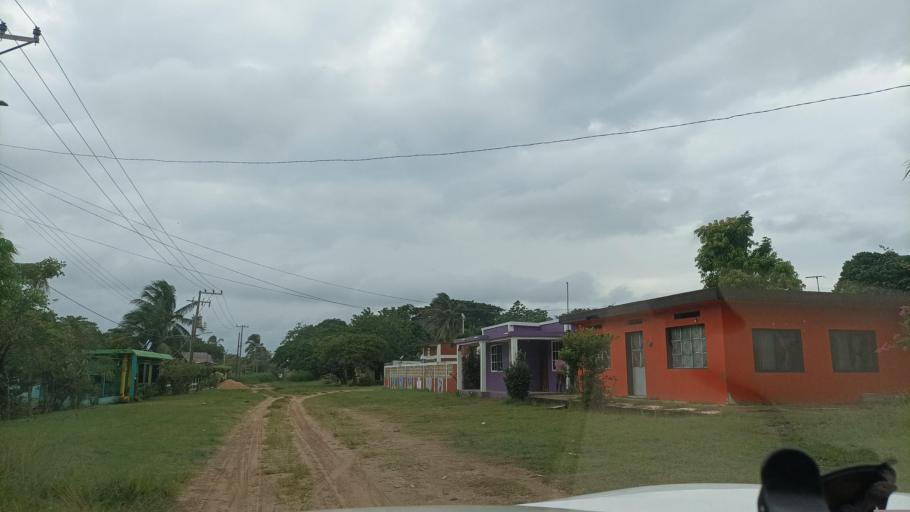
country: MX
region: Veracruz
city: Agua Dulce
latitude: 18.2079
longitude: -94.1383
